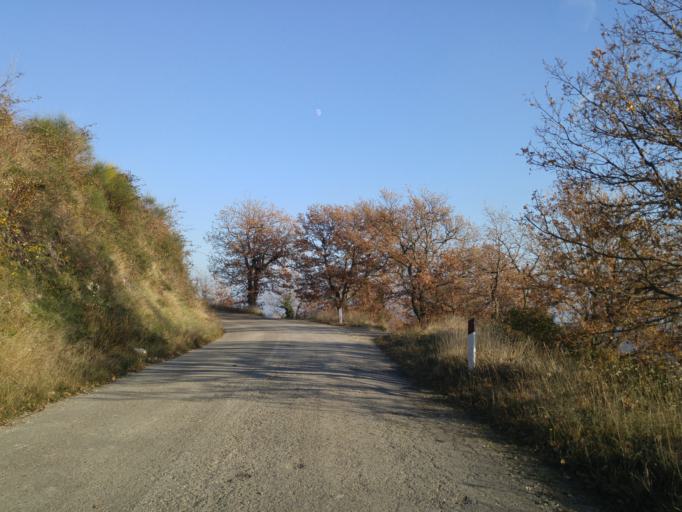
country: IT
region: The Marches
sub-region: Provincia di Pesaro e Urbino
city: Montefelcino
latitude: 43.7624
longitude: 12.8256
